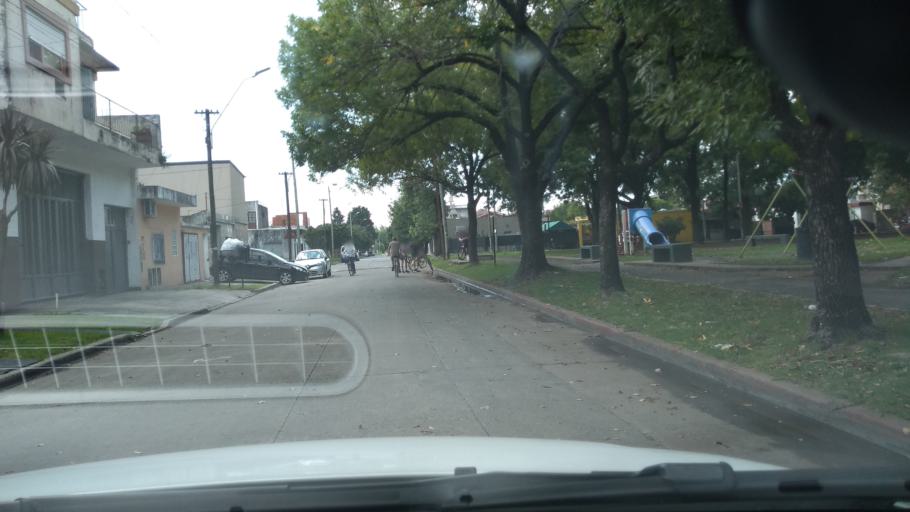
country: AR
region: Buenos Aires
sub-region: Partido de Moron
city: Moron
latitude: -34.6679
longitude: -58.6079
